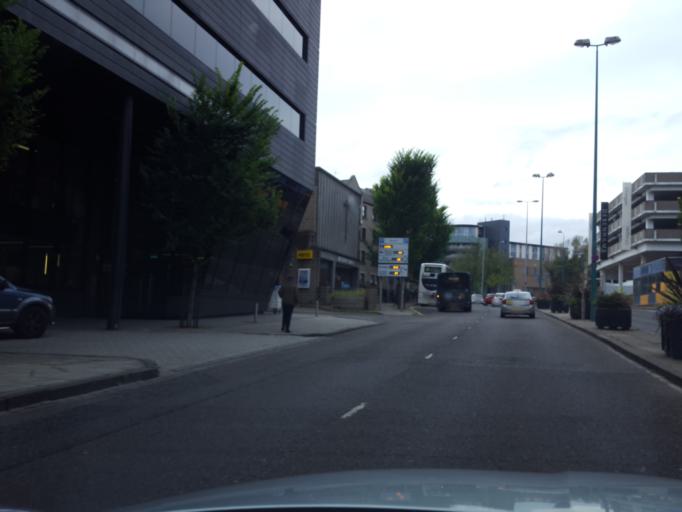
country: GB
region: Scotland
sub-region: Dundee City
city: Dundee
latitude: 56.4587
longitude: -2.9747
